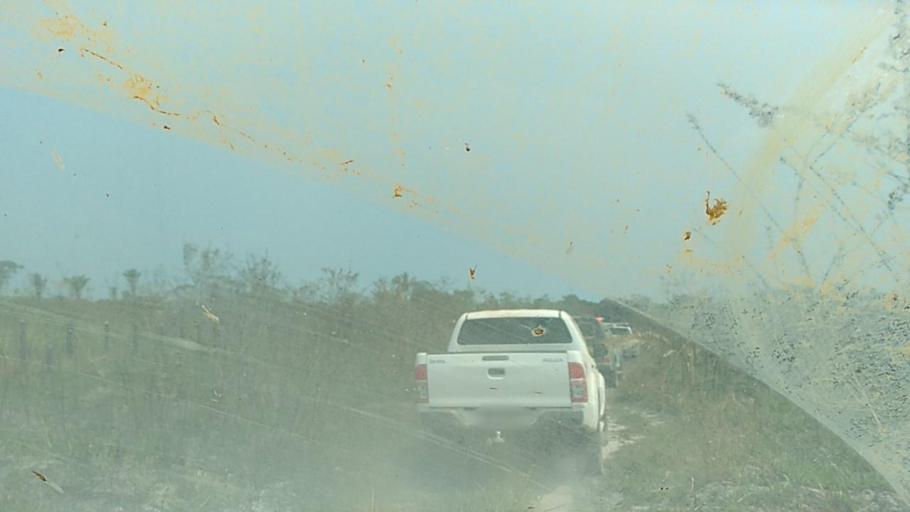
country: BR
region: Rondonia
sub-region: Porto Velho
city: Porto Velho
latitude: -8.9616
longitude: -64.3998
